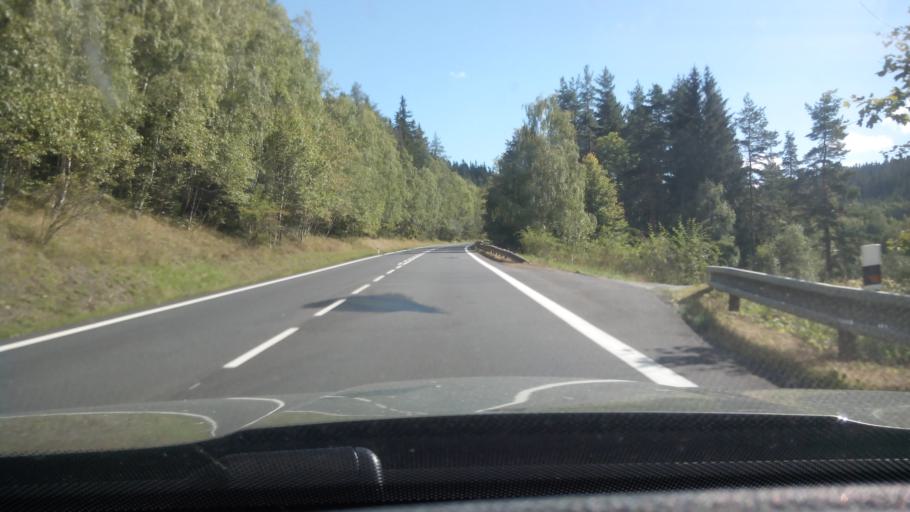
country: CZ
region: Jihocesky
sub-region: Okres Prachatice
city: Zdikov
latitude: 49.0737
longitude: 13.7099
